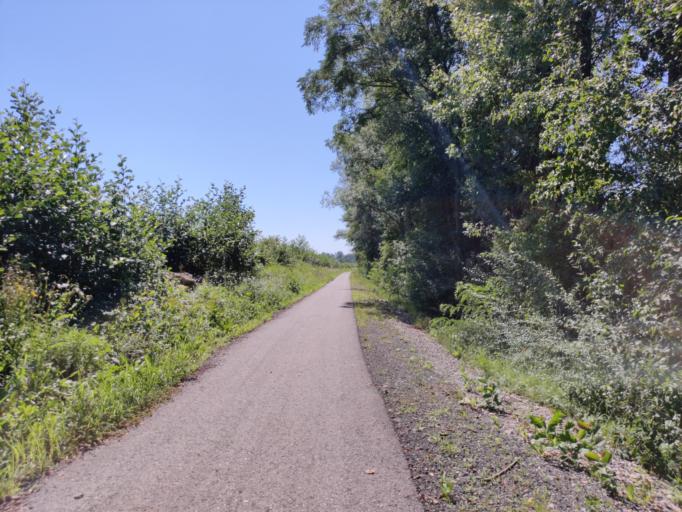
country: AT
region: Styria
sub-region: Politischer Bezirk Leibnitz
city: Stocking
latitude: 46.8819
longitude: 15.5251
